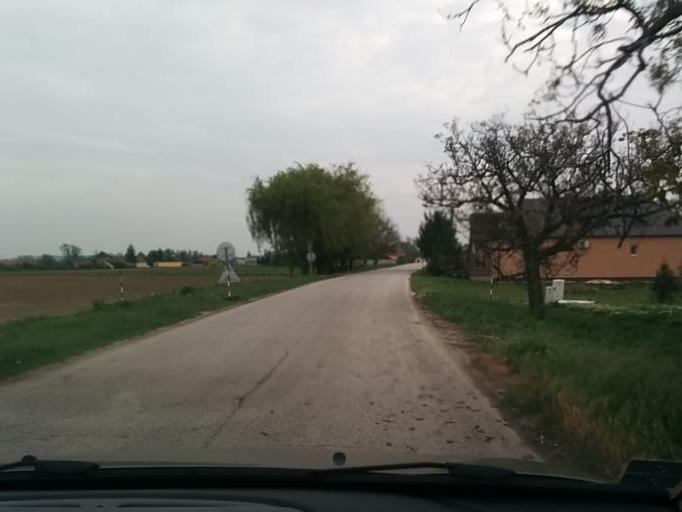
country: SK
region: Trnavsky
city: Sladkovicovo
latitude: 48.2111
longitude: 17.6522
